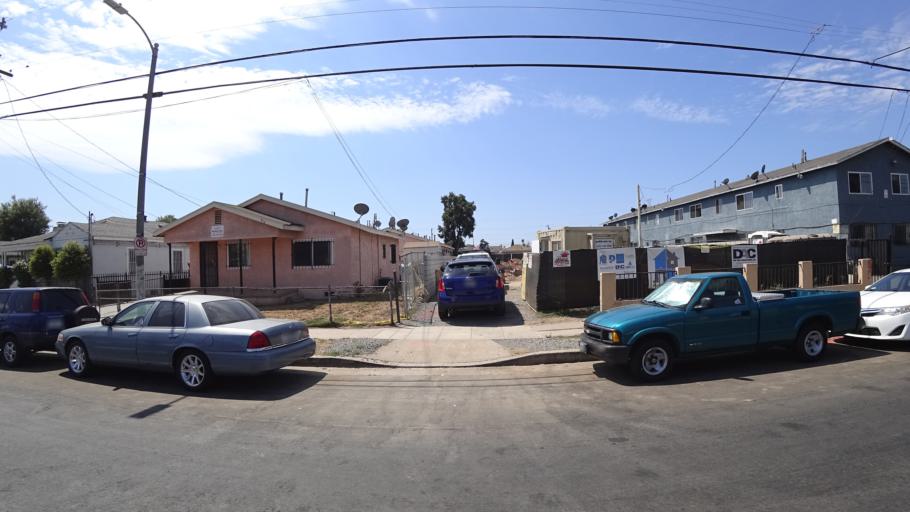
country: US
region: California
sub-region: Los Angeles County
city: Westmont
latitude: 33.9492
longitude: -118.2901
